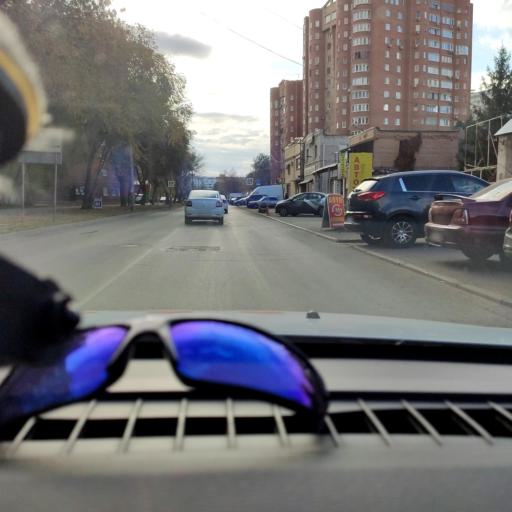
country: RU
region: Samara
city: Samara
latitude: 53.2484
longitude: 50.2103
